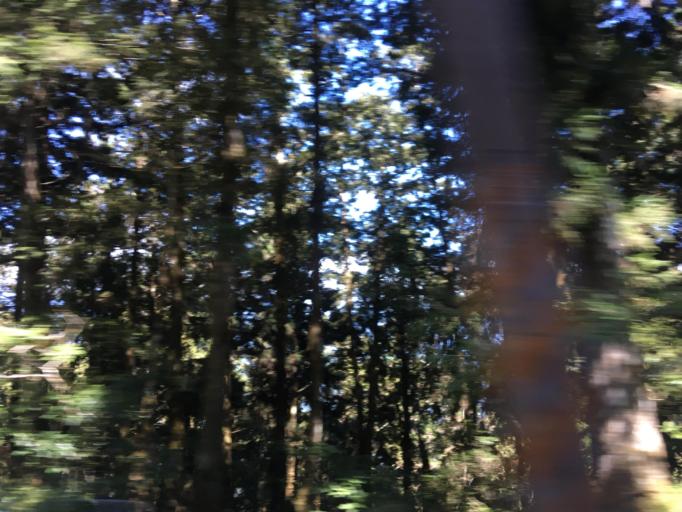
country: TW
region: Taiwan
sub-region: Yilan
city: Yilan
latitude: 24.5126
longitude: 121.5215
